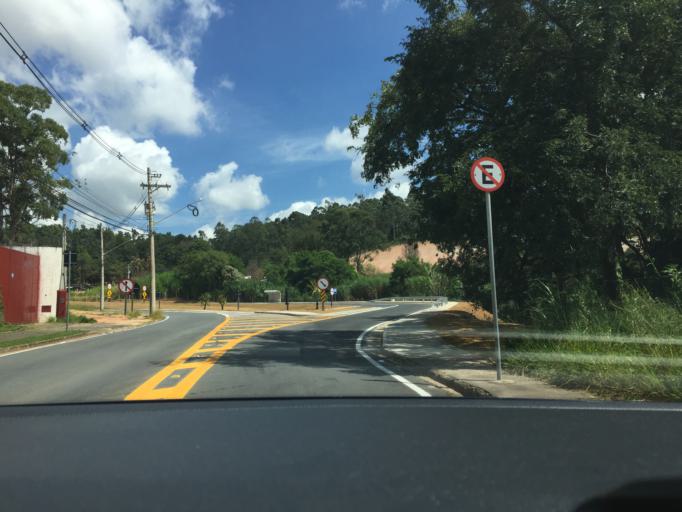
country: BR
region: Sao Paulo
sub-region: Jundiai
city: Jundiai
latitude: -23.1649
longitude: -46.8762
